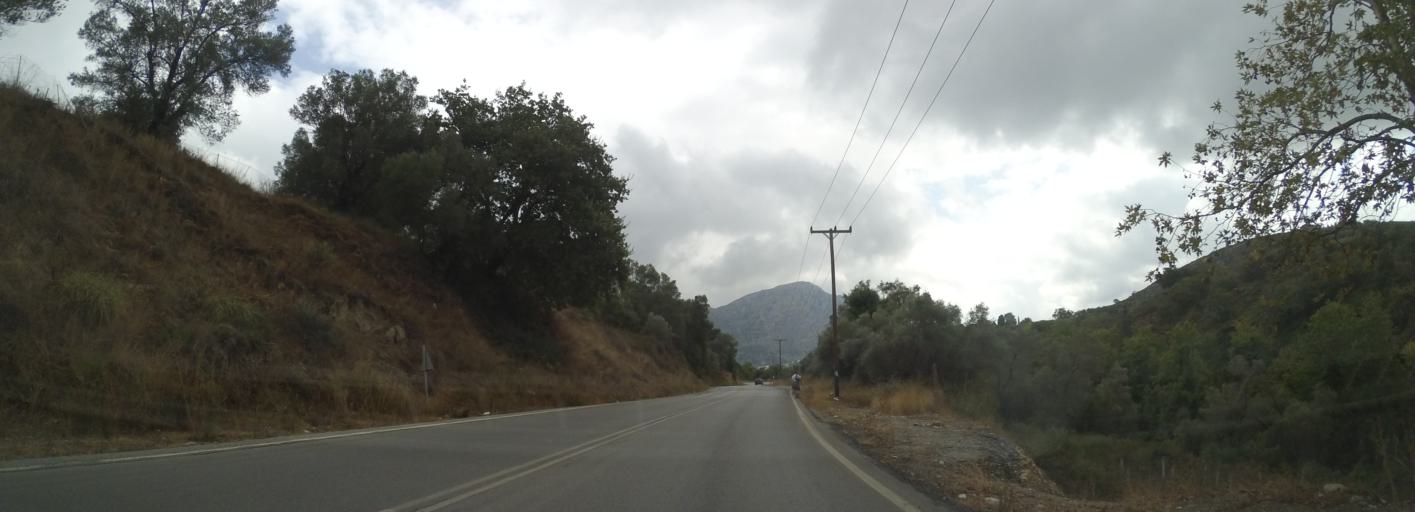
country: GR
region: Crete
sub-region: Nomos Rethymnis
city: Agia Foteini
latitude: 35.2207
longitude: 24.5143
